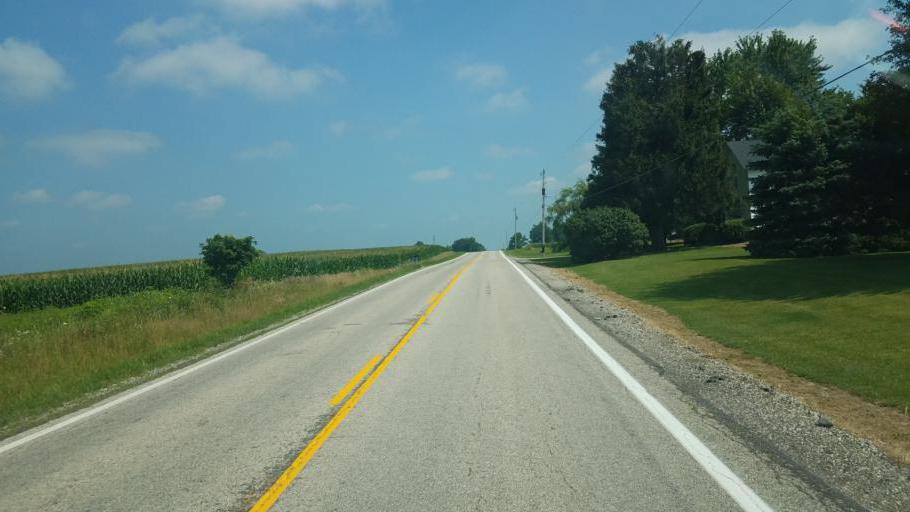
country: US
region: Ohio
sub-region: Crawford County
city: Bucyrus
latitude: 40.8999
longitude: -82.8547
